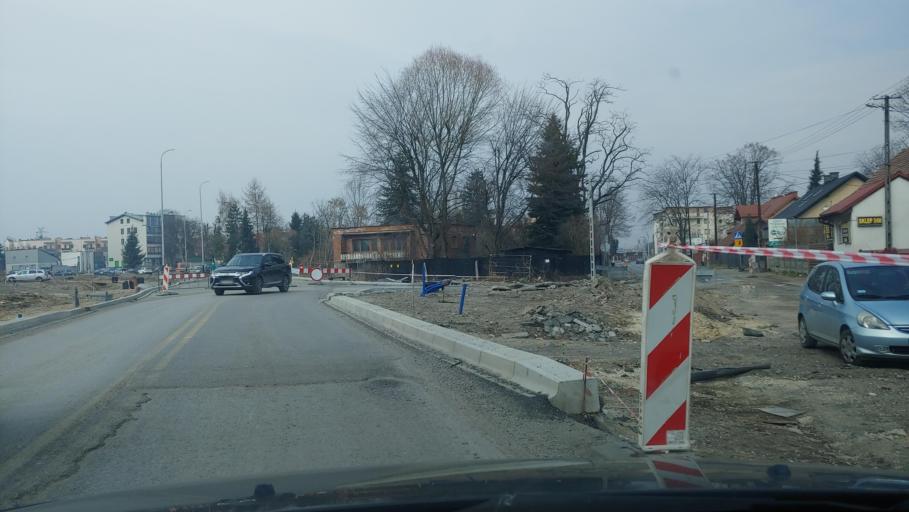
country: PL
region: Lesser Poland Voivodeship
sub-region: Powiat krakowski
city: Zielonki
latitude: 50.0949
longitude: 19.9355
